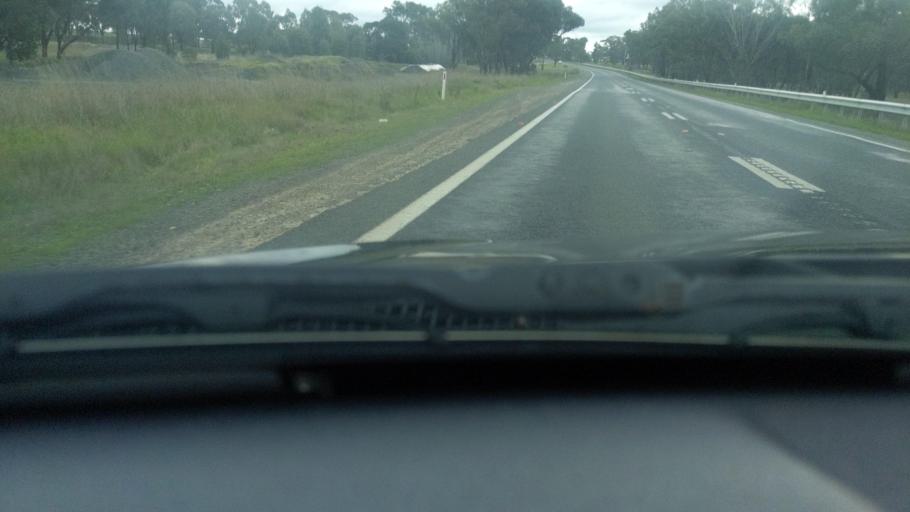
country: AU
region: New South Wales
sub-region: Wagga Wagga
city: Forest Hill
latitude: -35.1593
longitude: 147.5014
